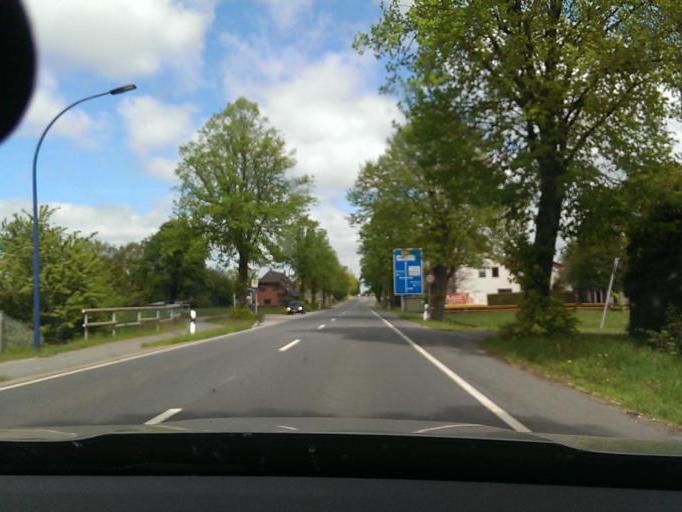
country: DE
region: Lower Saxony
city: Oyten
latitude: 53.0488
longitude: 9.0334
